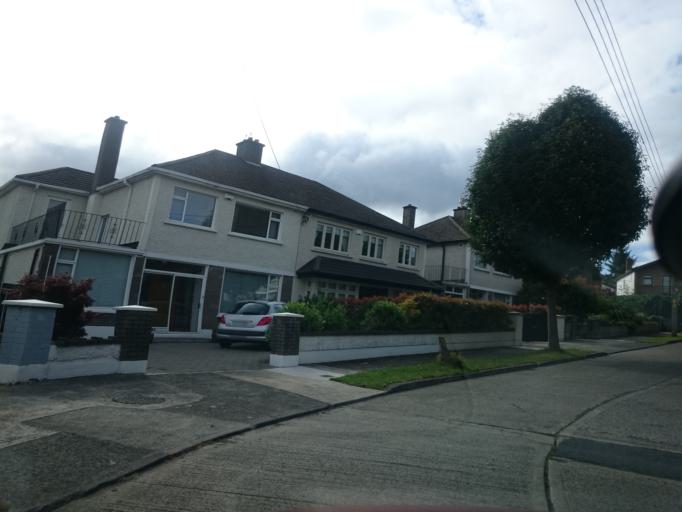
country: IE
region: Leinster
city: Mount Merrion
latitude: 53.2860
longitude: -6.2035
